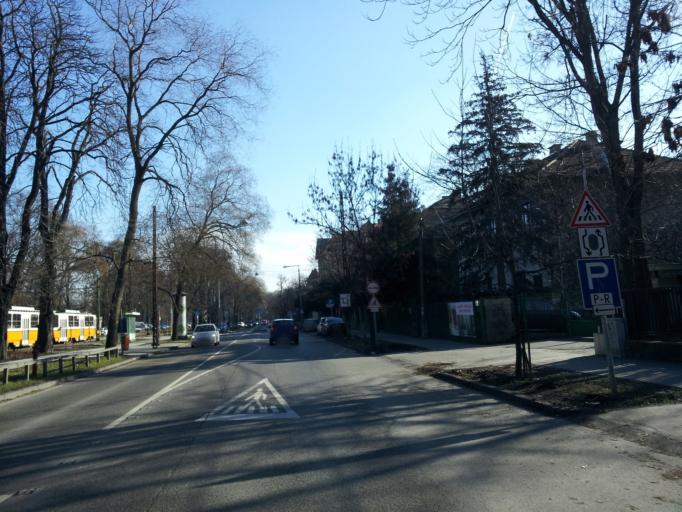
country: HU
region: Budapest
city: Budapest XII. keruelet
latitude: 47.5197
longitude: 18.9931
